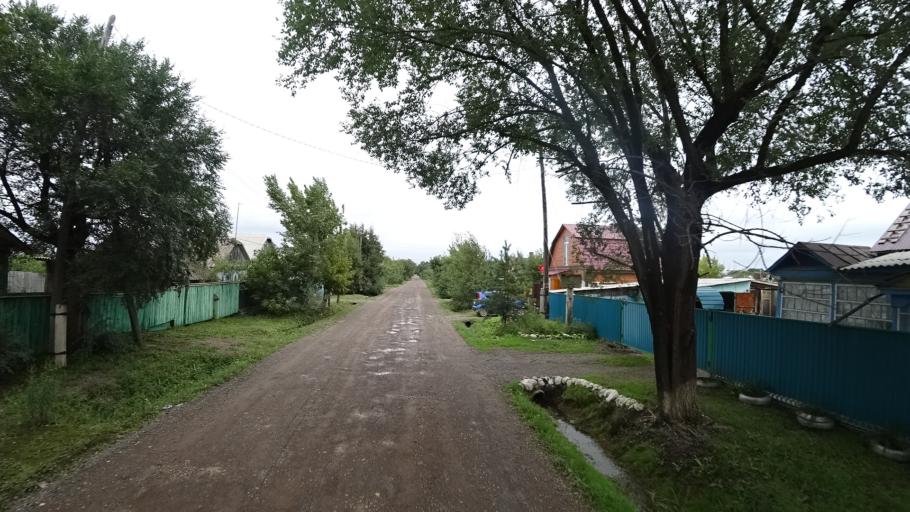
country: RU
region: Primorskiy
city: Chernigovka
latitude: 44.3372
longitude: 132.5646
